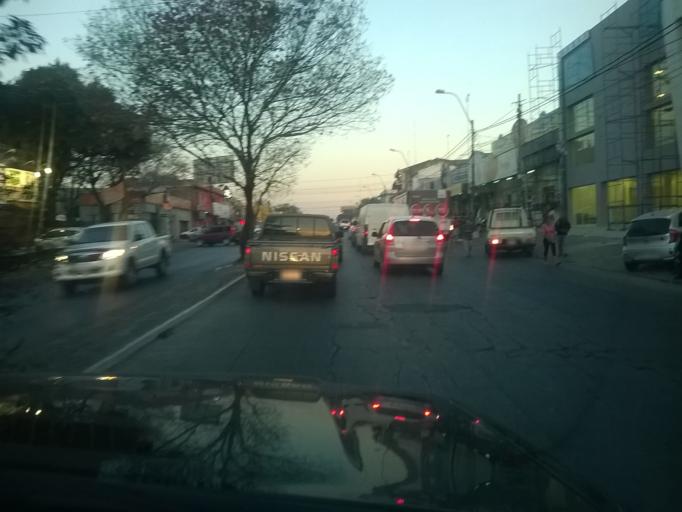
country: PY
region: Asuncion
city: Asuncion
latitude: -25.3045
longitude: -57.6090
